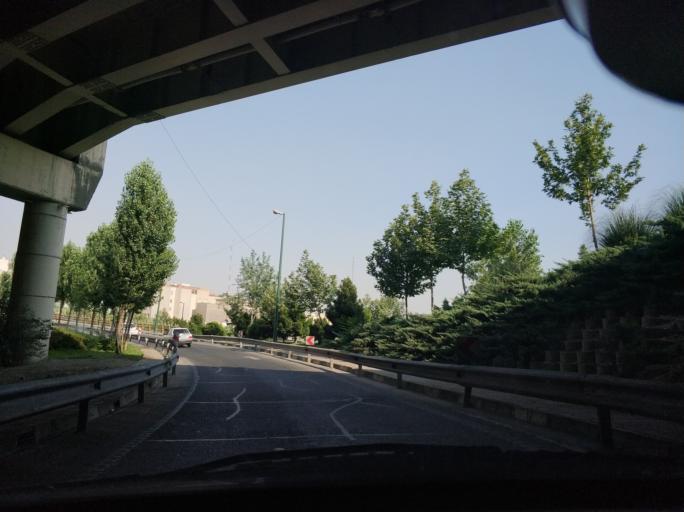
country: IR
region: Tehran
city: Tehran
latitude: 35.7395
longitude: 51.3684
